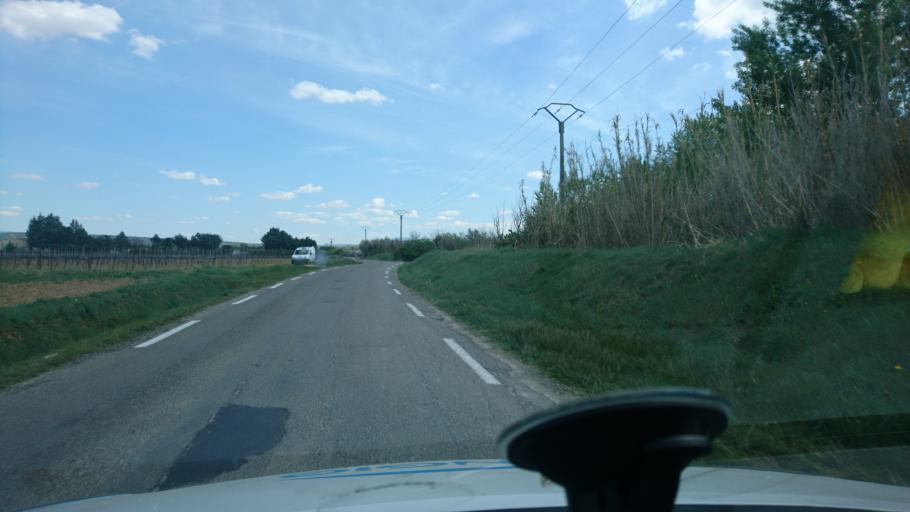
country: FR
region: Provence-Alpes-Cote d'Azur
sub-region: Departement du Vaucluse
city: Maubec
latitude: 43.8587
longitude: 5.1502
